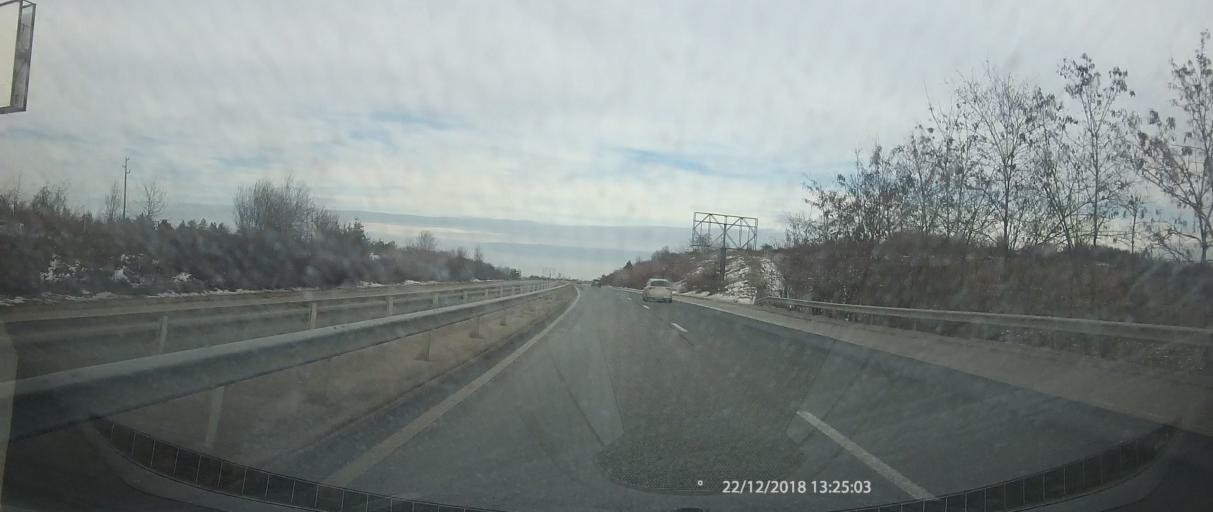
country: BG
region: Lovech
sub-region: Obshtina Yablanitsa
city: Yablanitsa
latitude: 43.0299
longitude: 24.1168
